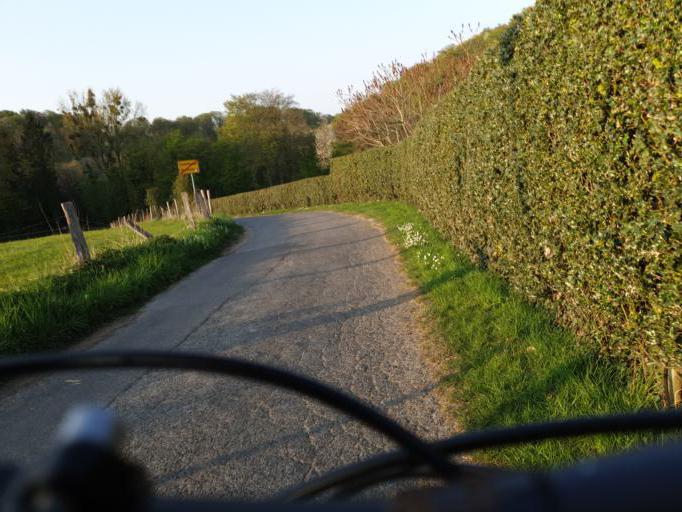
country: DE
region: North Rhine-Westphalia
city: Opladen
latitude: 51.0678
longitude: 7.0724
